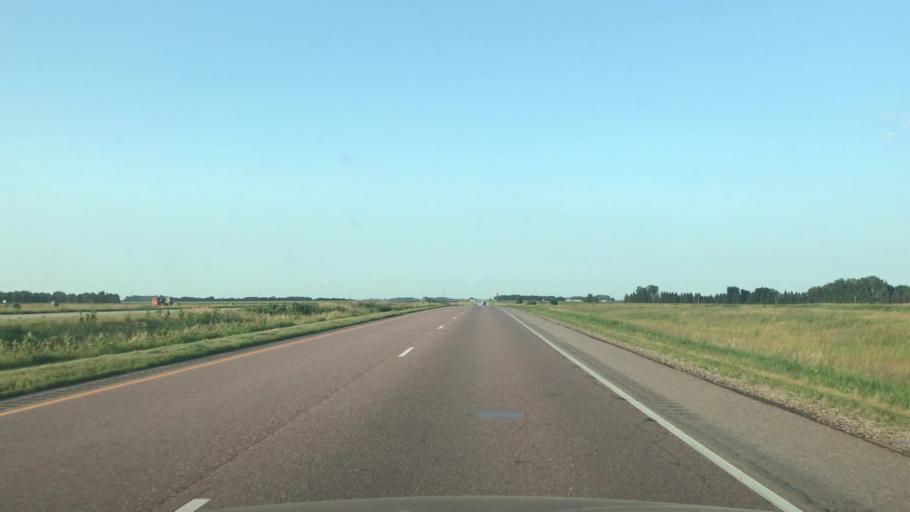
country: US
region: Minnesota
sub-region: Nobles County
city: Worthington
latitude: 43.7418
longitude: -95.4050
